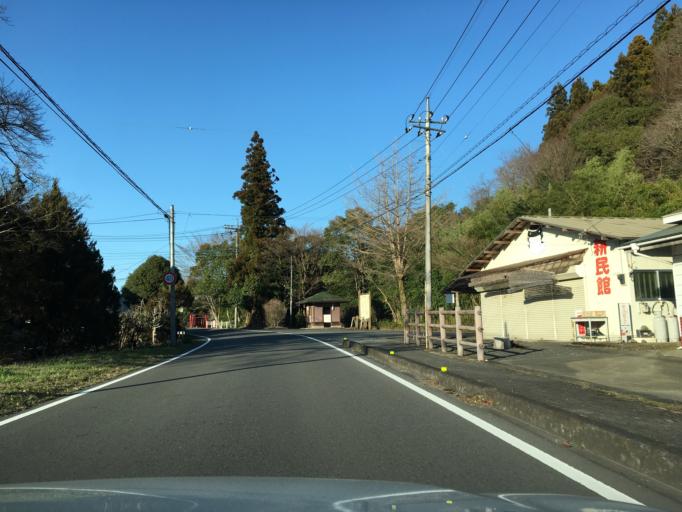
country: JP
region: Tochigi
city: Karasuyama
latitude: 36.7665
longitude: 140.2050
